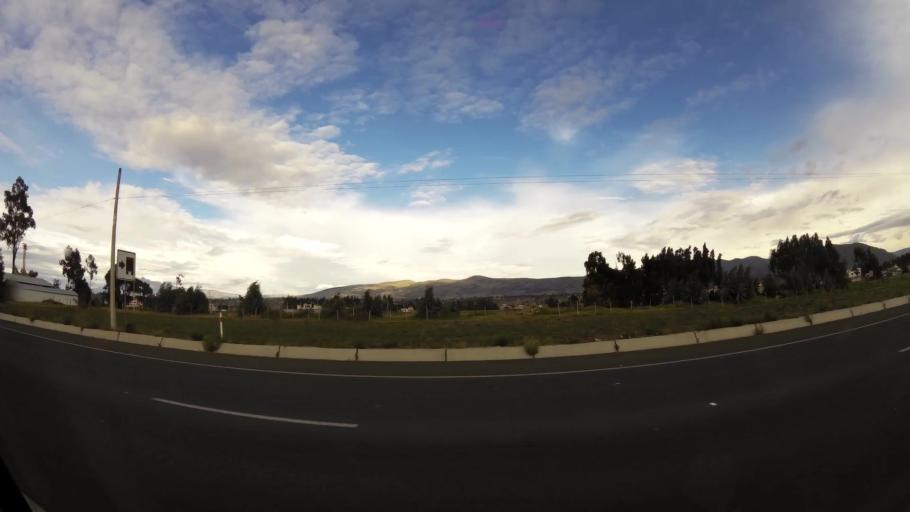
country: EC
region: Cotopaxi
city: Latacunga
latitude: -0.9095
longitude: -78.6279
